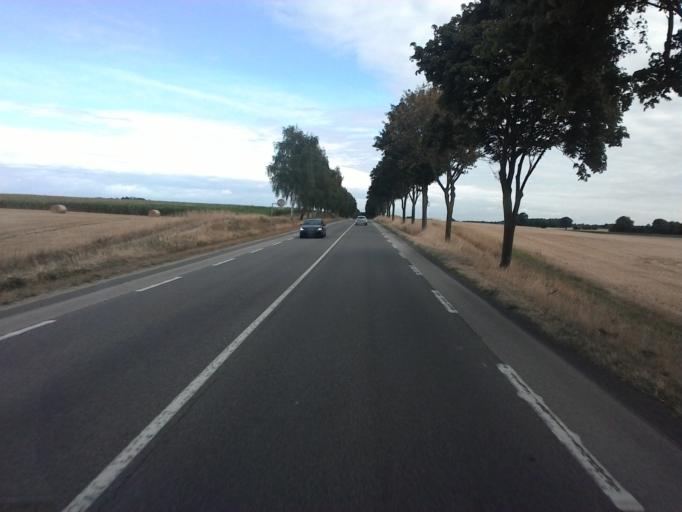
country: FR
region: Rhone-Alpes
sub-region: Departement de l'Ain
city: Saint-Martin-du-Mont
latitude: 46.1106
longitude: 5.3026
